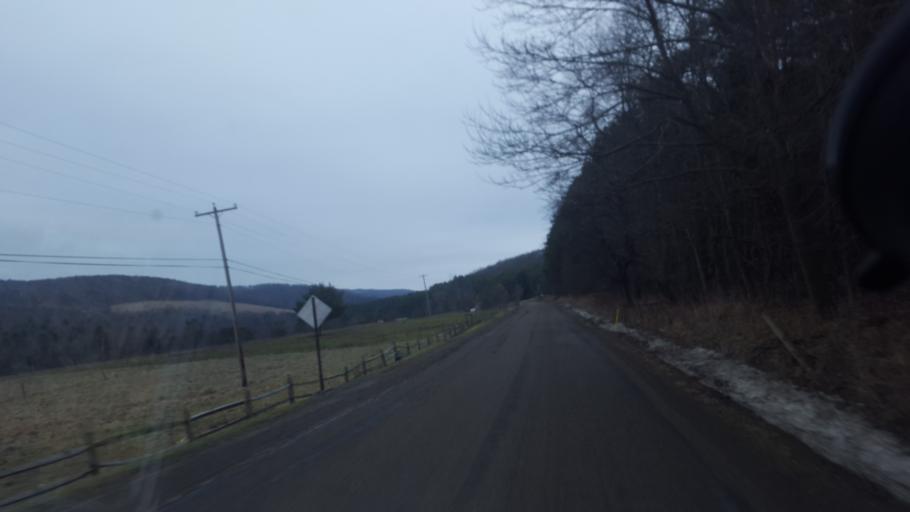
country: US
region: New York
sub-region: Allegany County
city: Wellsville
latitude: 41.9595
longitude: -77.8404
